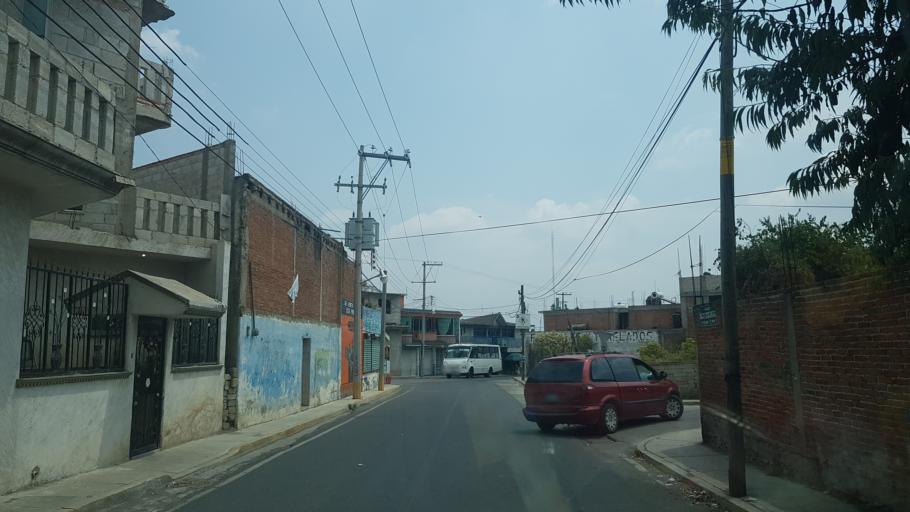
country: MX
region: Puebla
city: Domingo Arenas
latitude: 19.1416
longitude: -98.4587
